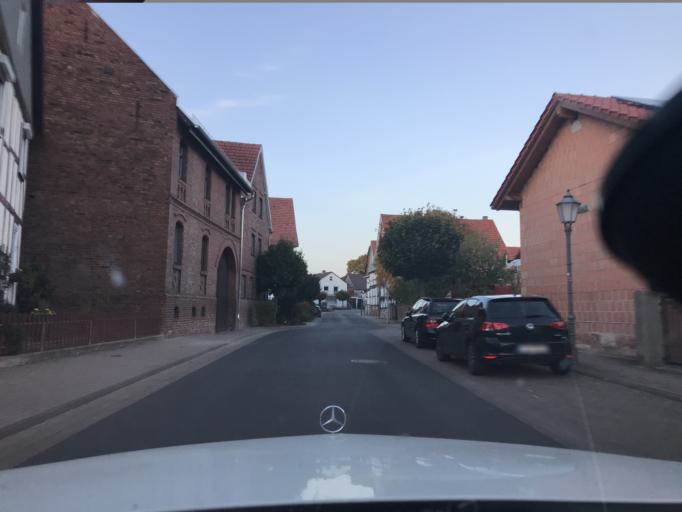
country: DE
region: Hesse
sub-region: Regierungsbezirk Kassel
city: Eschwege
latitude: 51.1530
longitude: 9.9960
